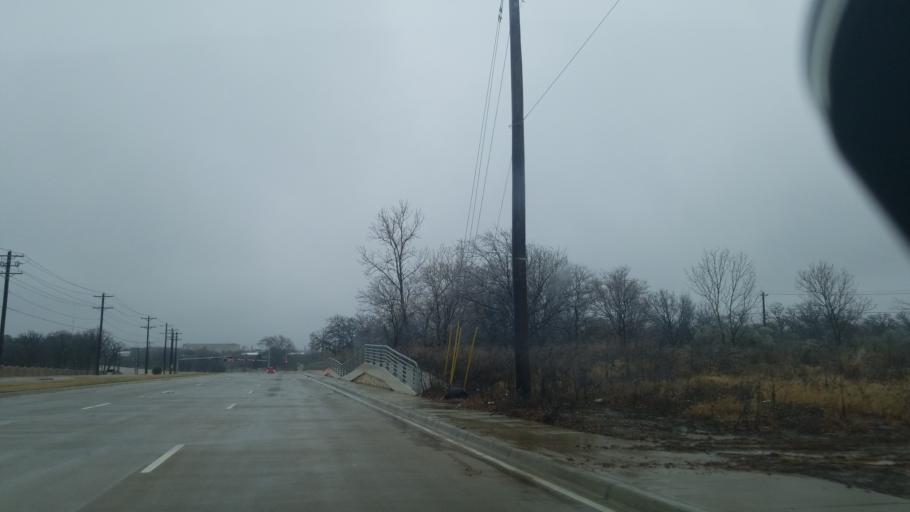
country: US
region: Texas
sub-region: Denton County
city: Corinth
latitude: 33.1628
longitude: -97.0923
